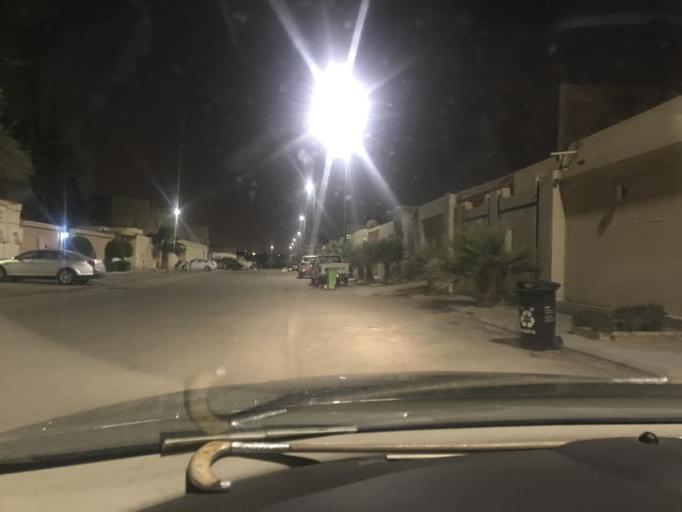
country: SA
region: Ar Riyad
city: Riyadh
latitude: 24.7336
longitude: 46.7796
